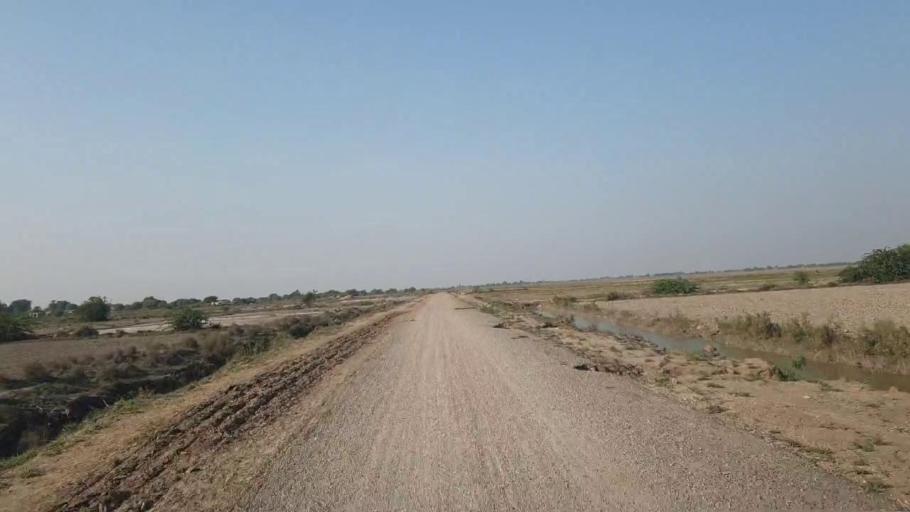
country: PK
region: Sindh
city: Kario
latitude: 24.9041
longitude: 68.6203
